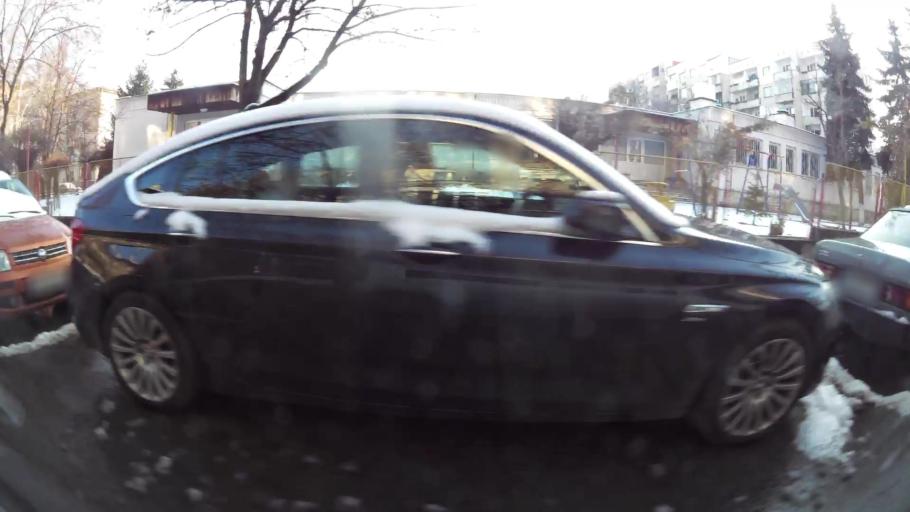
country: BG
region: Sofia-Capital
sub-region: Stolichna Obshtina
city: Sofia
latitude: 42.6837
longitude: 23.3573
